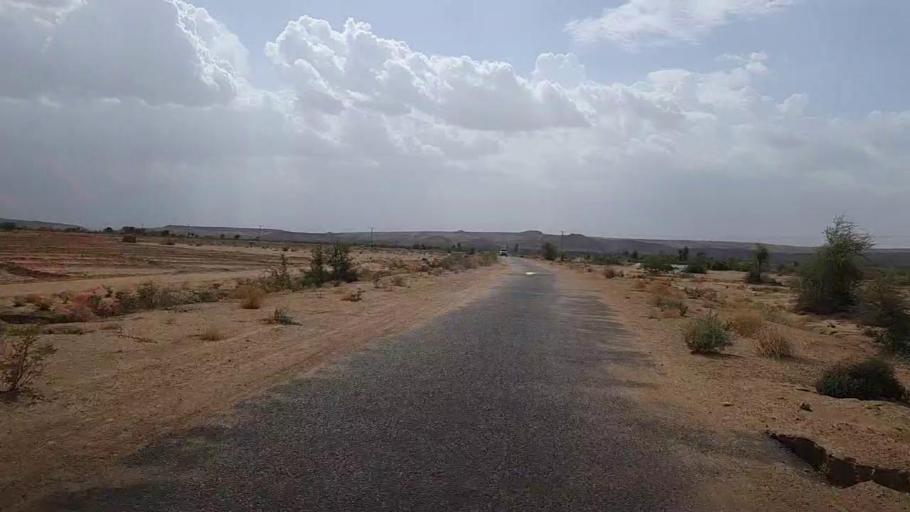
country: PK
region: Sindh
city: Jamshoro
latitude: 25.4028
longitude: 67.7731
